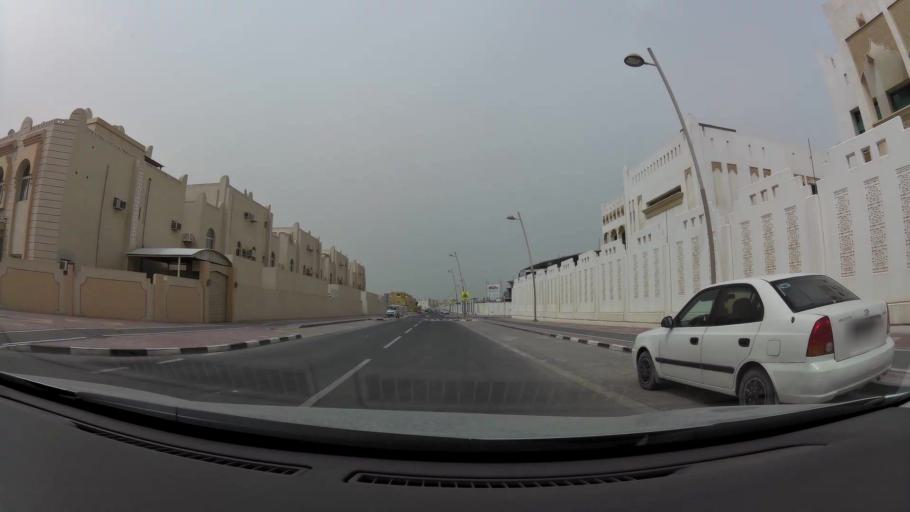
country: QA
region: Baladiyat ad Dawhah
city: Doha
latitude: 25.2353
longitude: 51.5438
